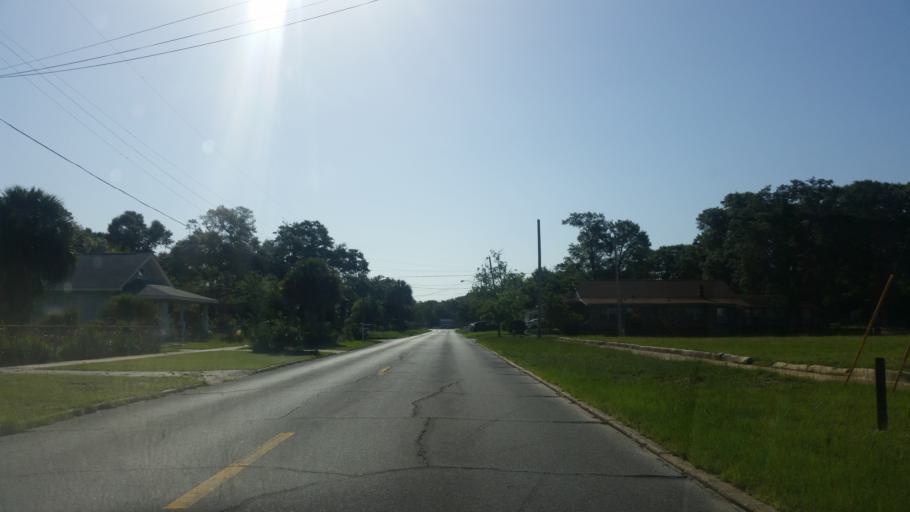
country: US
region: Florida
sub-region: Escambia County
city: Pensacola
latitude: 30.4139
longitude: -87.2290
